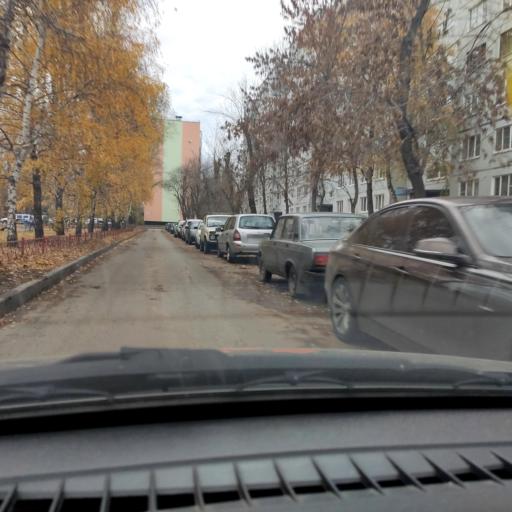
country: RU
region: Samara
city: Tol'yatti
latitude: 53.5103
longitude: 49.2940
